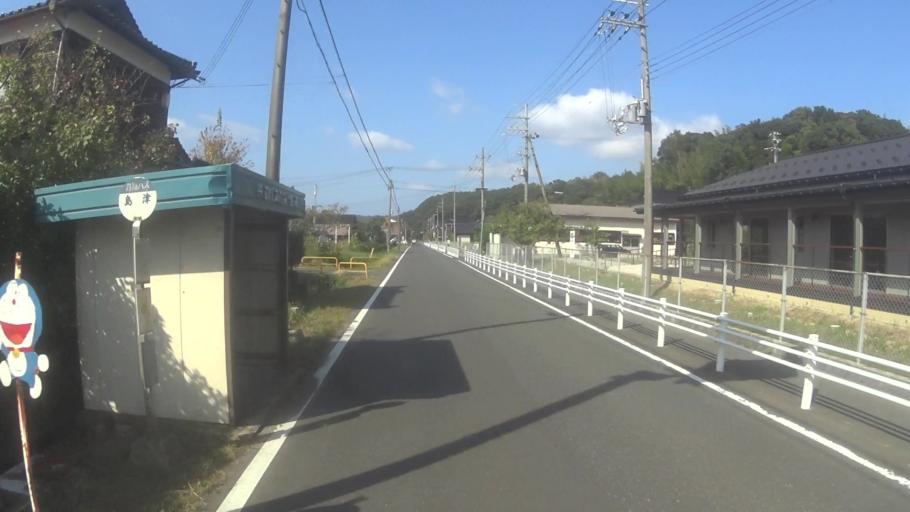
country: JP
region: Kyoto
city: Miyazu
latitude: 35.6824
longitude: 135.0521
